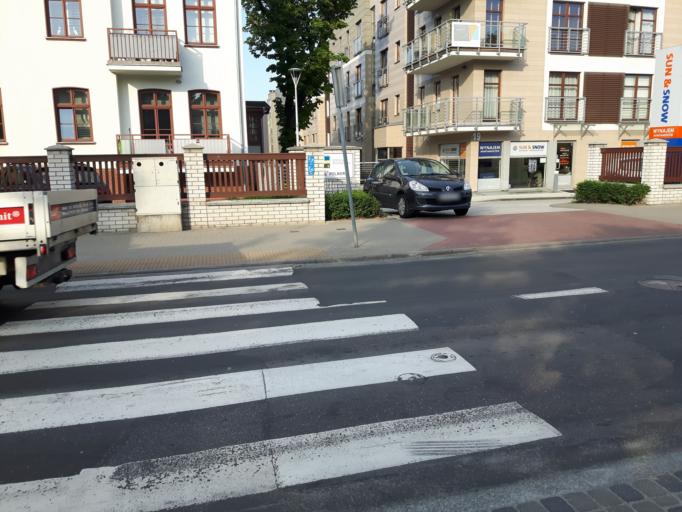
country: PL
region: Pomeranian Voivodeship
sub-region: Sopot
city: Sopot
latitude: 54.4335
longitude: 18.5709
